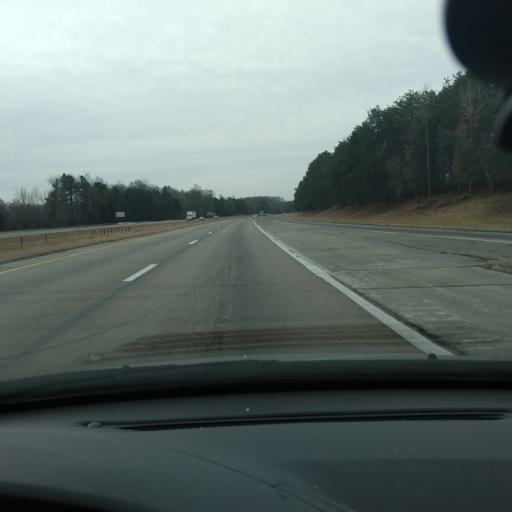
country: US
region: North Carolina
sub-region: Davidson County
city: Midway
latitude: 35.9671
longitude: -80.2298
